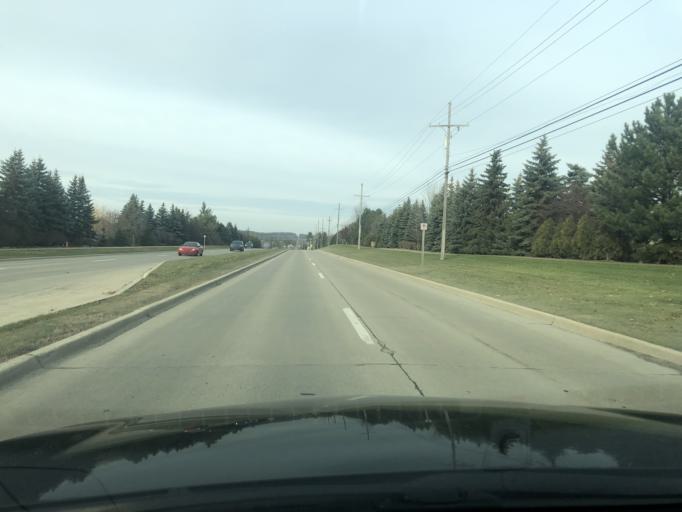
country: US
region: Michigan
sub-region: Wayne County
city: Northville
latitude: 42.4046
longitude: -83.5107
